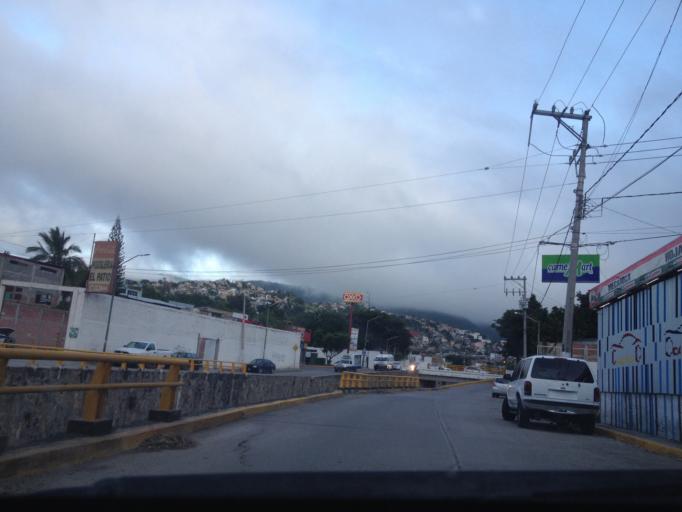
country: MX
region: Guerrero
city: Chilpancingo de los Bravos
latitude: 17.5492
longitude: -99.5033
